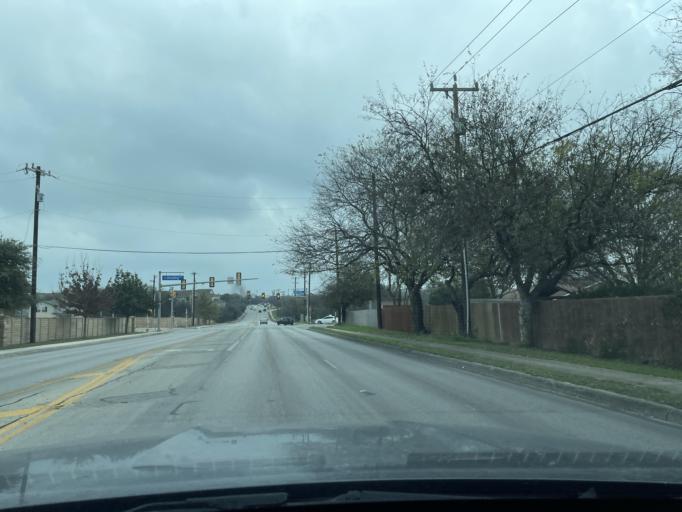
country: US
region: Texas
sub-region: Bexar County
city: Leon Valley
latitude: 29.5572
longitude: -98.6211
